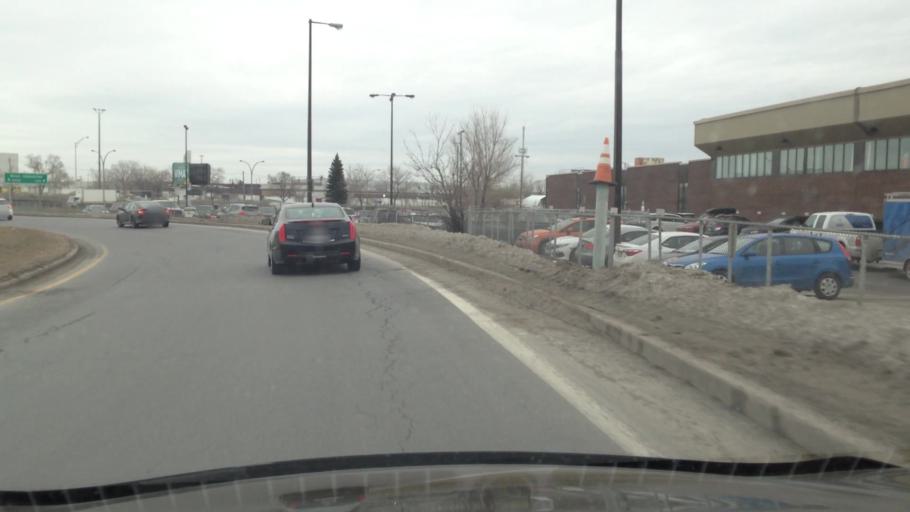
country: CA
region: Quebec
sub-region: Laval
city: Laval
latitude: 45.5830
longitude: -73.7363
